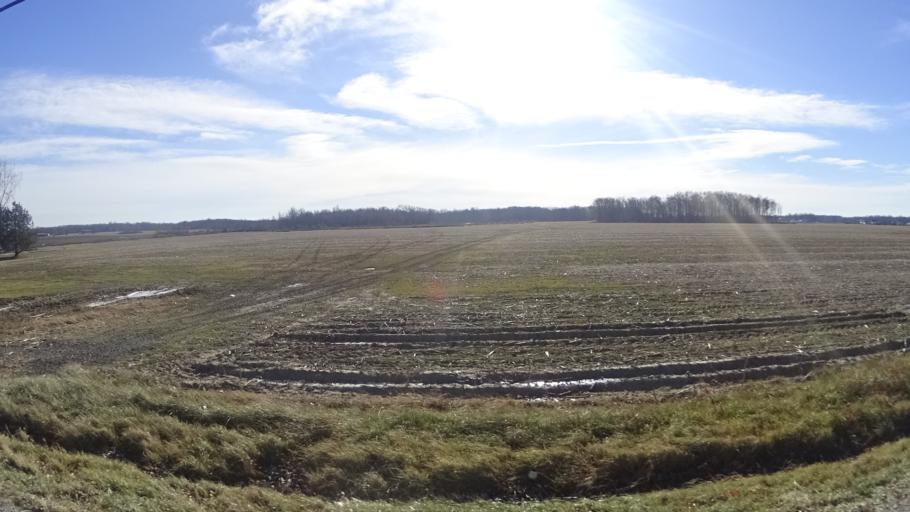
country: US
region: Ohio
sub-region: Lorain County
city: South Amherst
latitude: 41.3394
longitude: -82.3124
